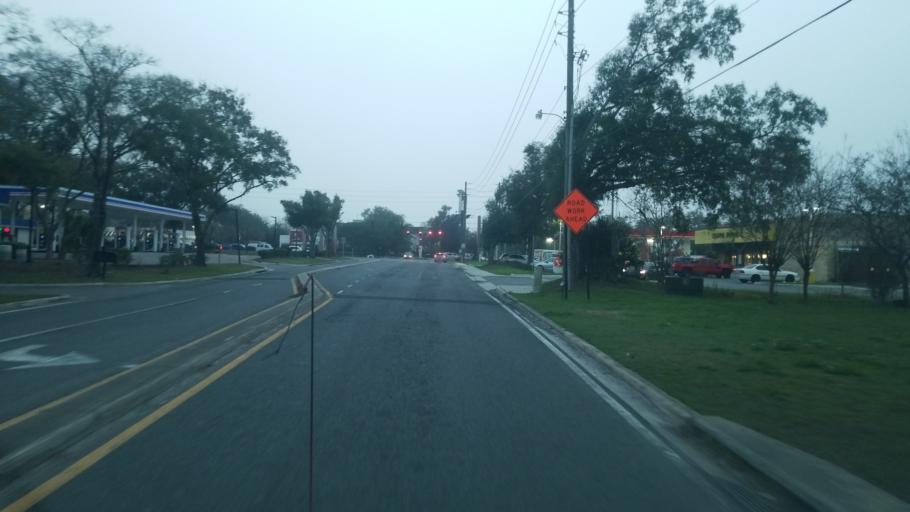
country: US
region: Florida
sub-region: Marion County
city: Ocala
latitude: 29.1490
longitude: -82.1884
